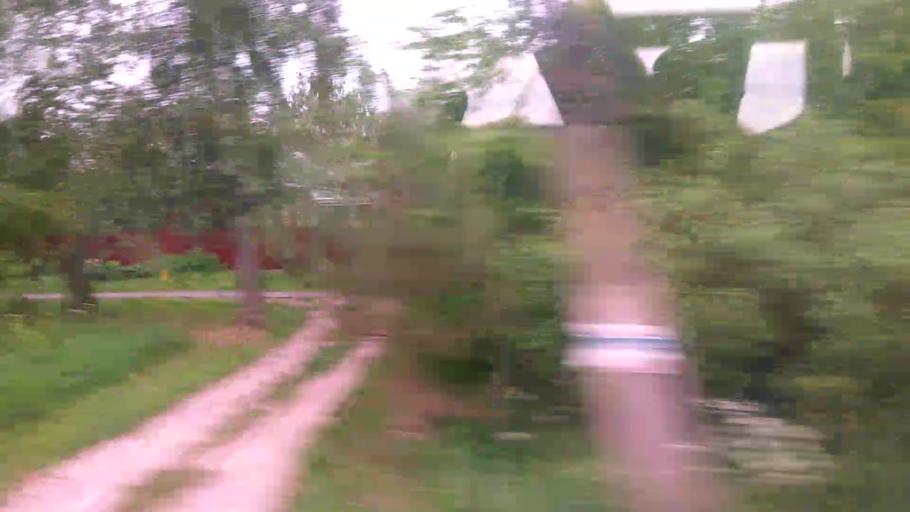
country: RU
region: Moskovskaya
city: Lukhovitsy
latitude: 54.9272
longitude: 39.0013
